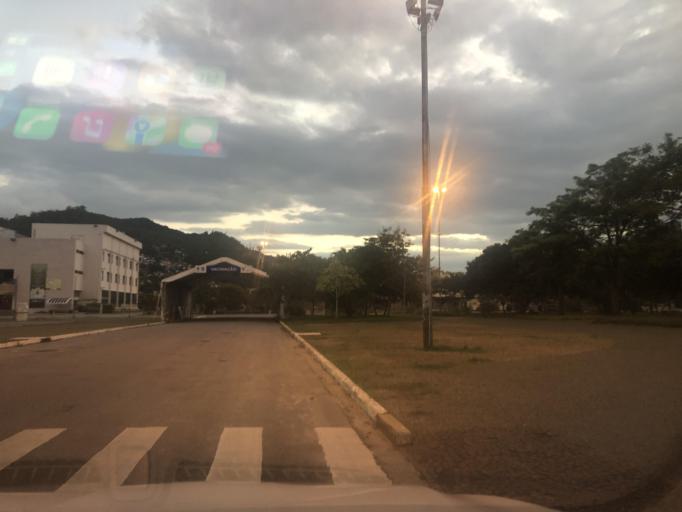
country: BR
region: Santa Catarina
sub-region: Florianopolis
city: Carvoeira
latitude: -27.6009
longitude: -48.5207
